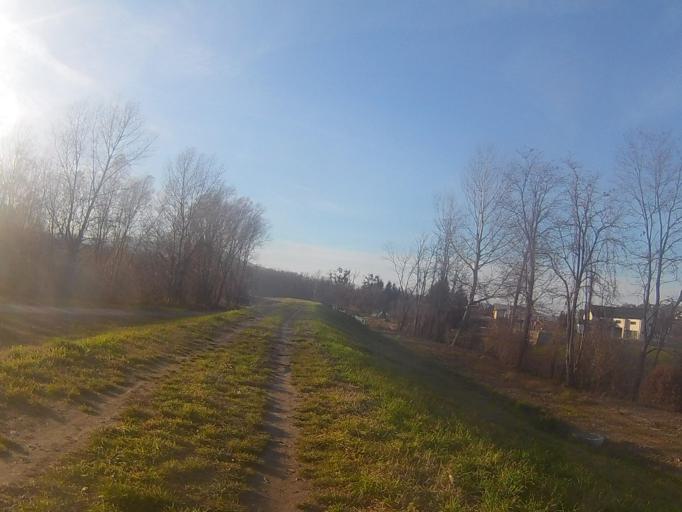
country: SI
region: Duplek
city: Zgornji Duplek
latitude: 46.5060
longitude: 15.7304
